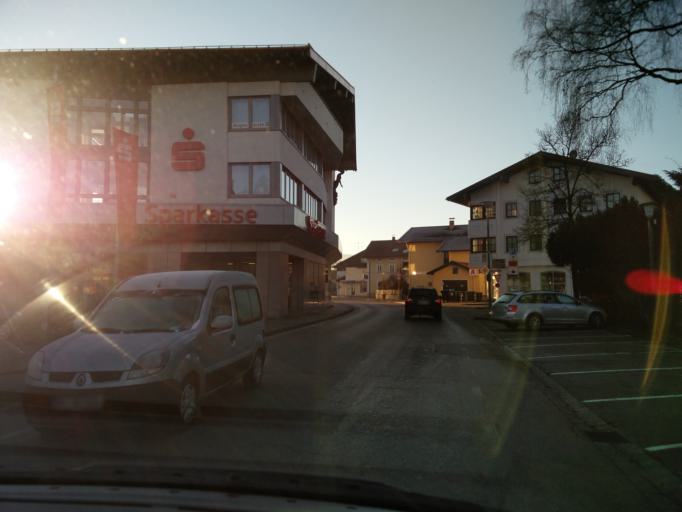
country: DE
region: Bavaria
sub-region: Upper Bavaria
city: Prien am Chiemsee
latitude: 47.8541
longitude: 12.3465
